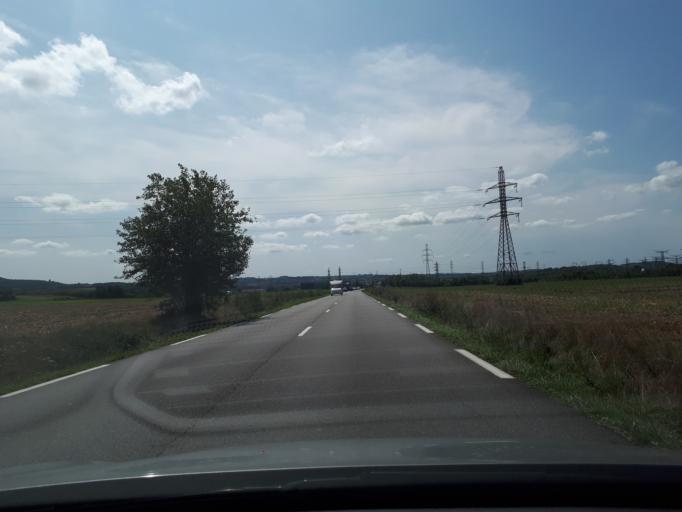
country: FR
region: Rhone-Alpes
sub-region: Departement de l'Isere
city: La Verpilliere
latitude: 45.6645
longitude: 5.1378
